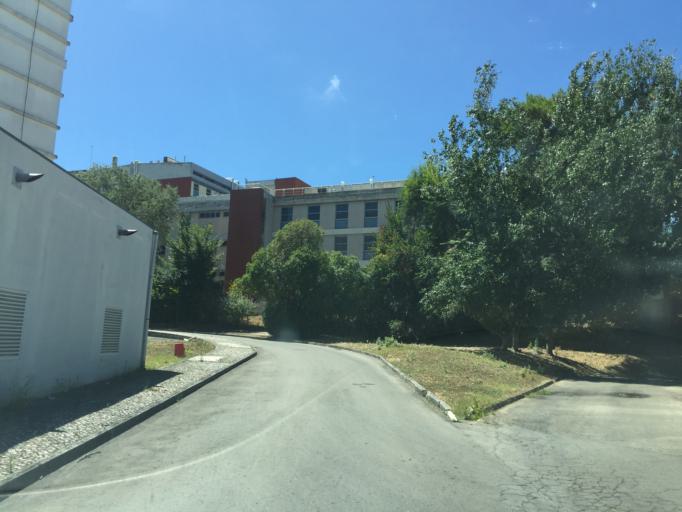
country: PT
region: Lisbon
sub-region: Odivelas
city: Olival do Basto
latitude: 38.7659
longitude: -9.1631
